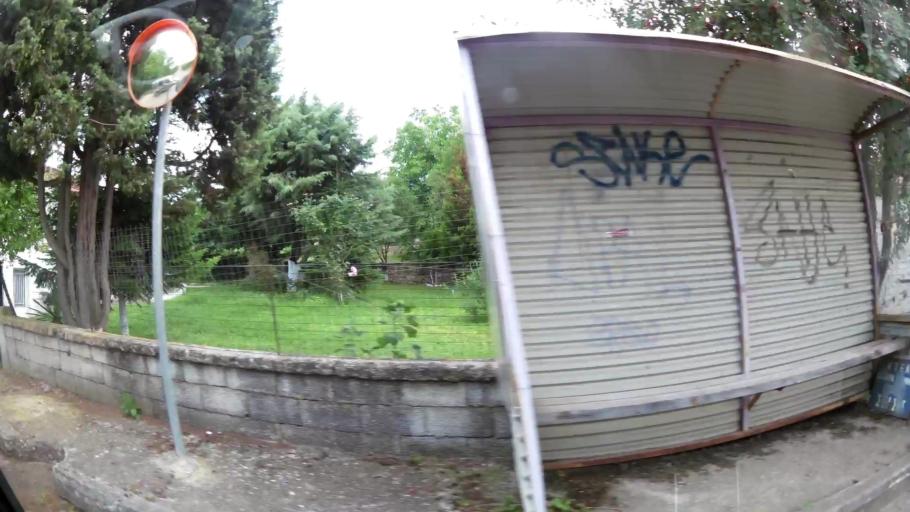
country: GR
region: West Macedonia
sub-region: Nomos Kozanis
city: Koila
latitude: 40.3494
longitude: 21.8327
